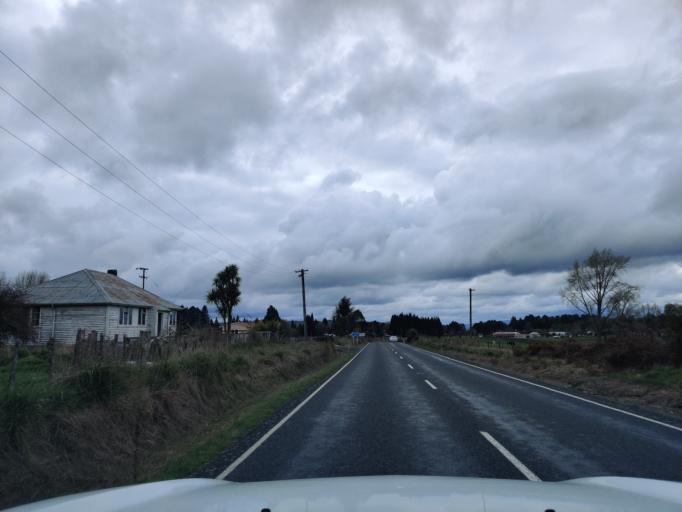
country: NZ
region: Waikato
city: Turangi
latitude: -39.0059
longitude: 175.3769
